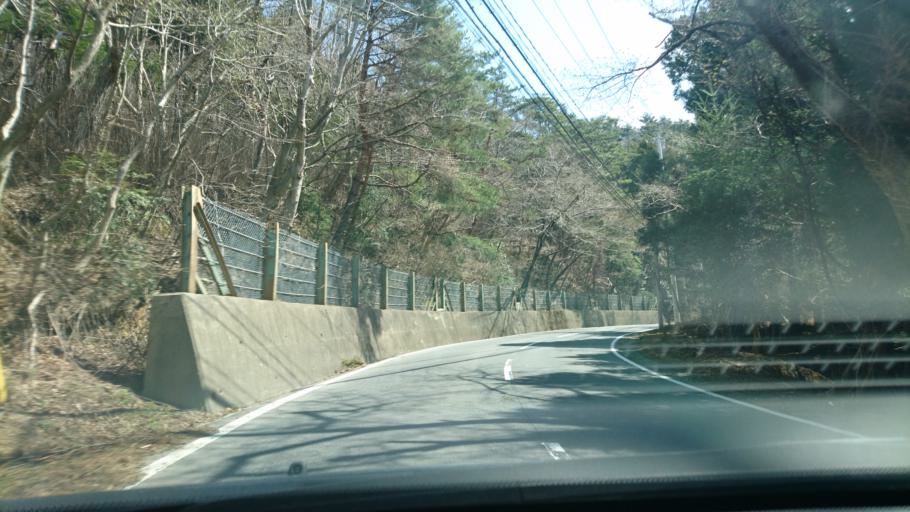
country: JP
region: Miyagi
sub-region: Oshika Gun
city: Onagawa Cho
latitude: 38.4420
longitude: 141.4804
